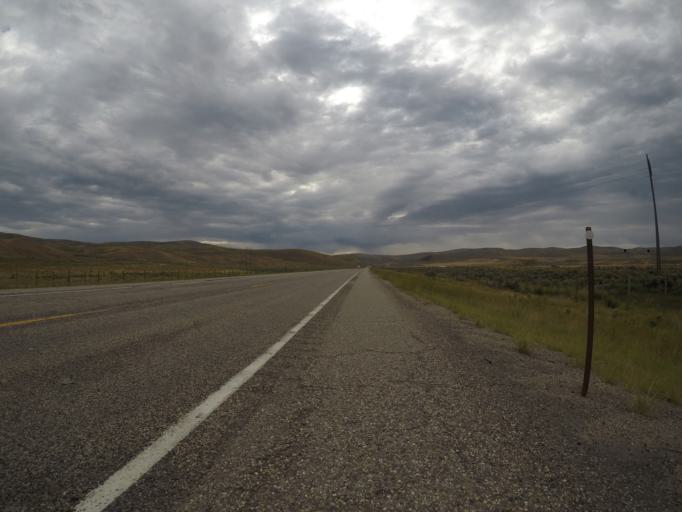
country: US
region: Utah
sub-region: Rich County
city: Randolph
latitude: 41.8239
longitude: -110.9026
